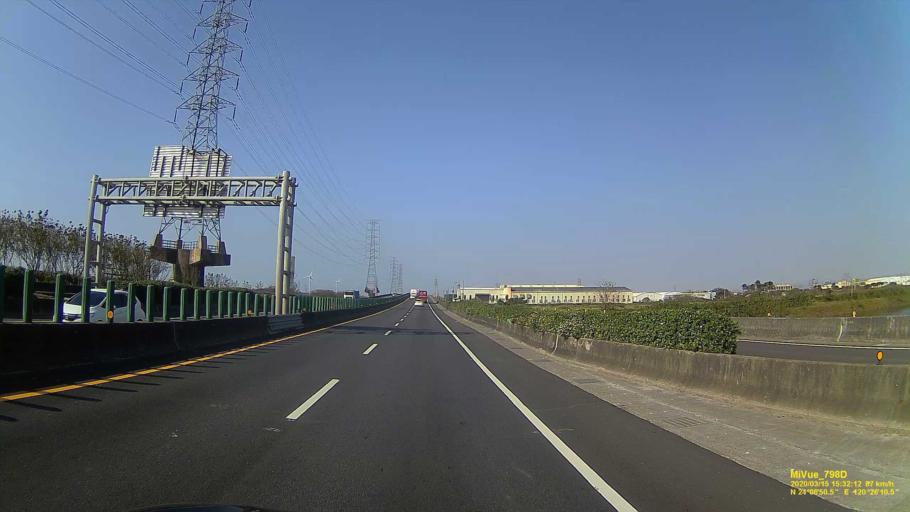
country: TW
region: Taiwan
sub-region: Changhua
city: Chang-hua
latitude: 24.1146
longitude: 120.4364
